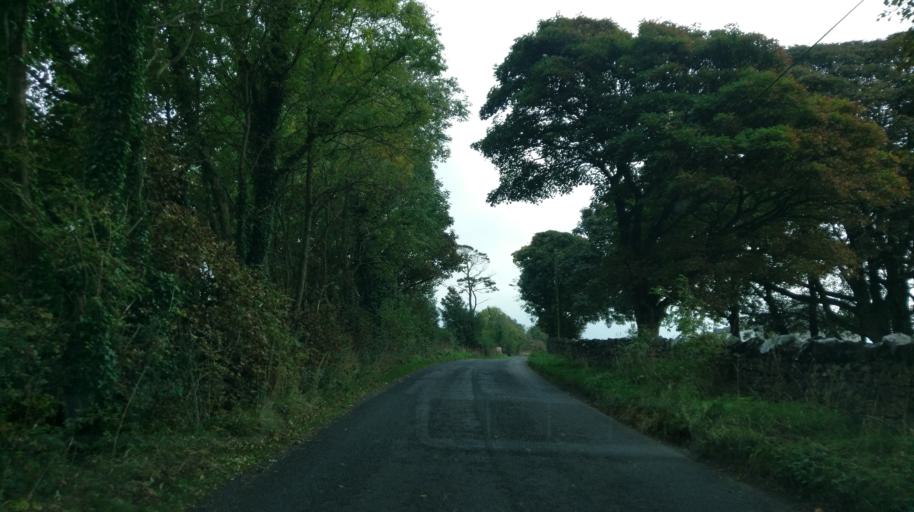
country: IE
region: Connaught
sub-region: County Galway
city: Athenry
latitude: 53.4532
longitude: -8.5832
